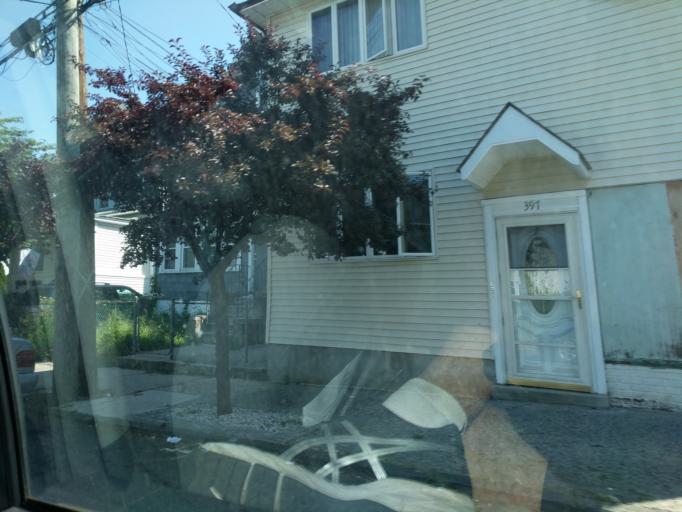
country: US
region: New Jersey
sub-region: Hudson County
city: Bayonne
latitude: 40.6315
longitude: -74.1166
